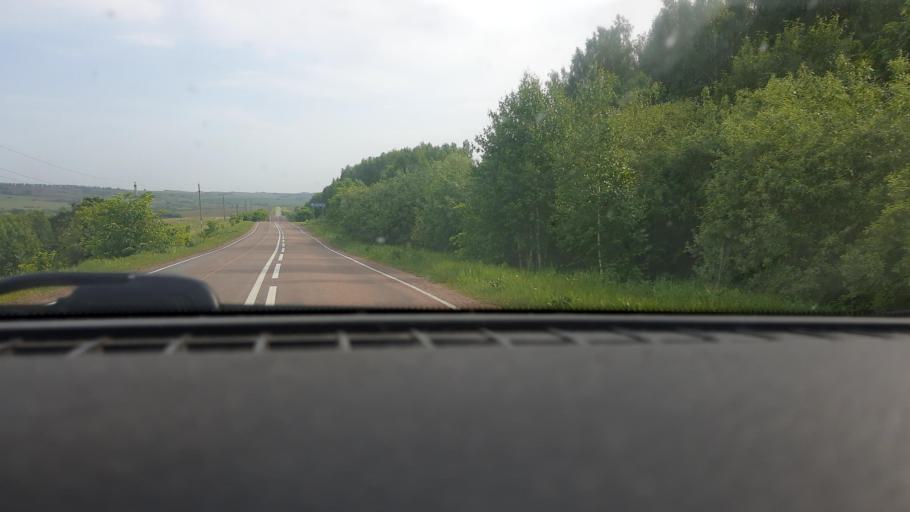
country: RU
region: Bashkortostan
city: Ulukulevo
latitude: 54.5535
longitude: 56.4349
